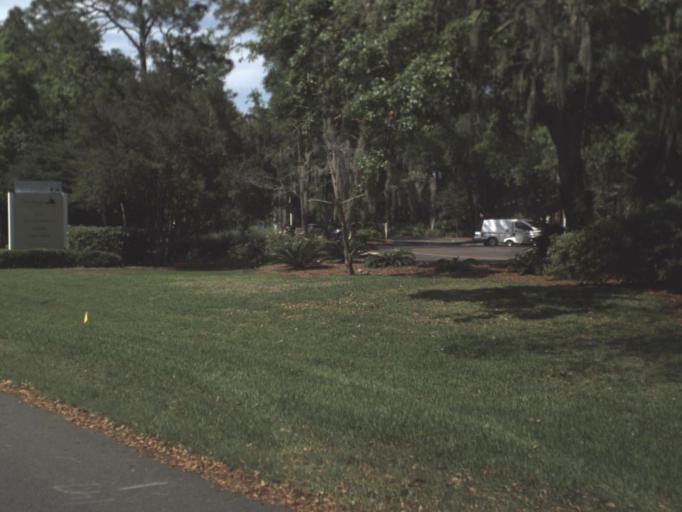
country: US
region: Florida
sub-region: Nassau County
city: Fernandina Beach
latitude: 30.5563
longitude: -81.4497
